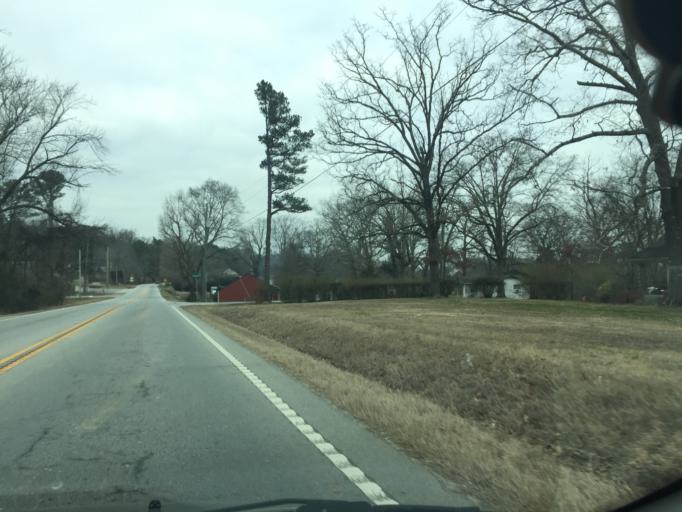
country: US
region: Georgia
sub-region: Catoosa County
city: Indian Springs
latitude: 34.9679
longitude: -85.1821
